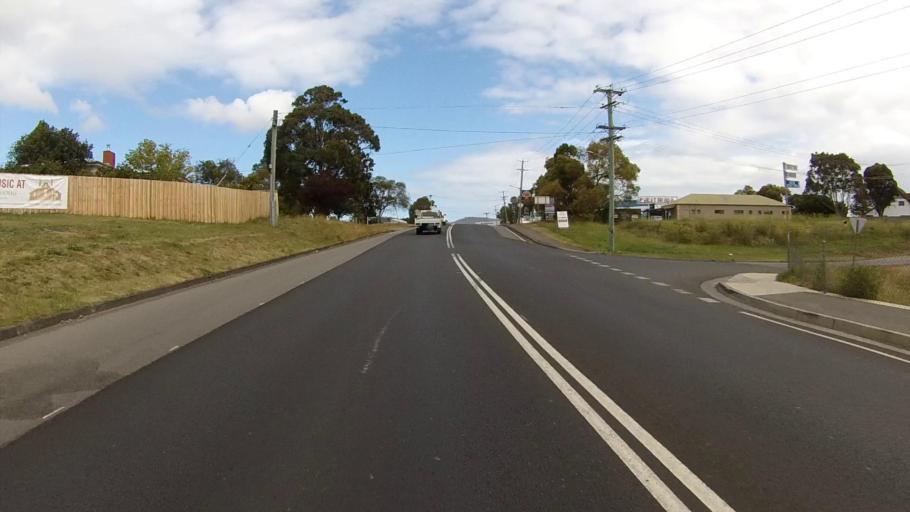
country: AU
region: Tasmania
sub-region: Clarence
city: Rokeby
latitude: -42.8994
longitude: 147.4440
